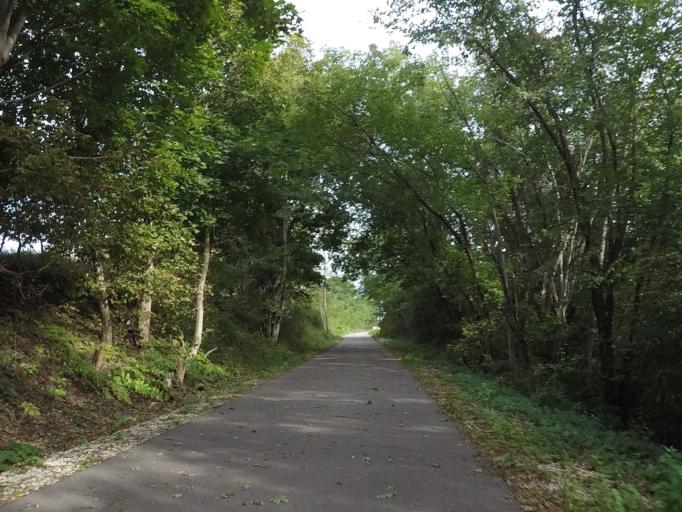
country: US
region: Wisconsin
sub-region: Sauk County
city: Prairie du Sac
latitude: 43.2874
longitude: -89.7181
